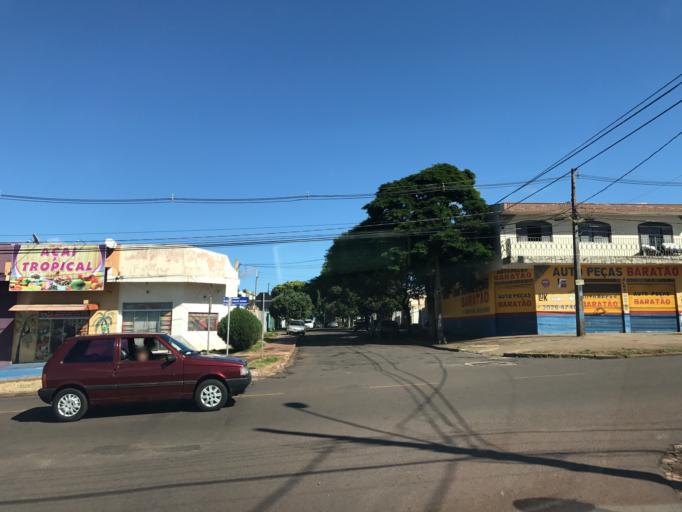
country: BR
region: Parana
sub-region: Maringa
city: Maringa
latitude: -23.4480
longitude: -51.9544
